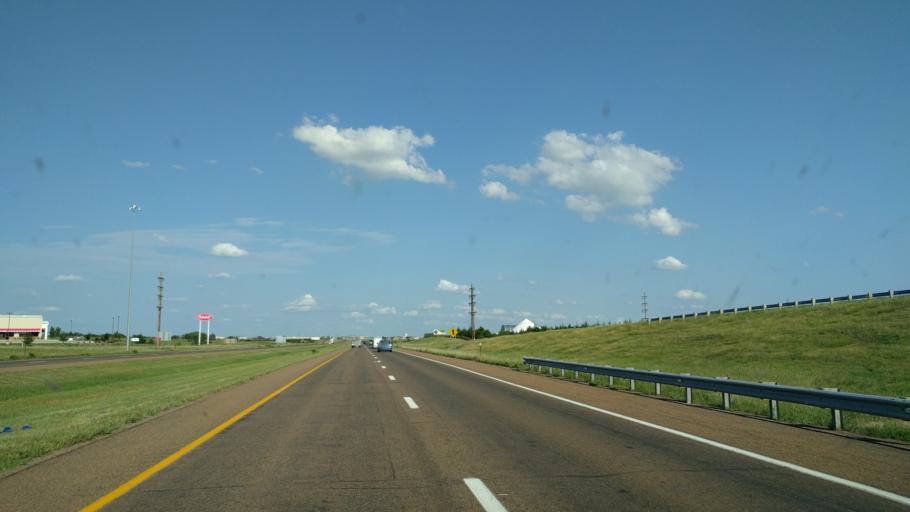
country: US
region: Kansas
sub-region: Ellis County
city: Hays
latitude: 38.9122
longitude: -99.3543
